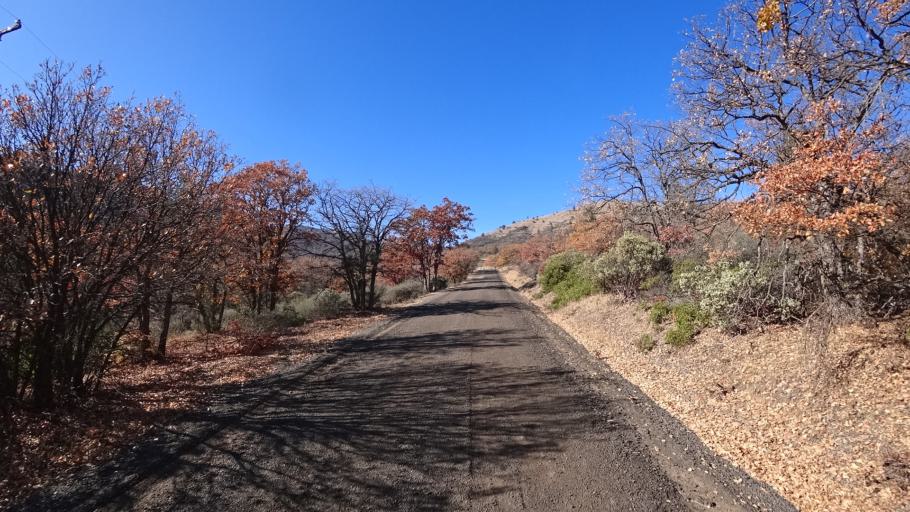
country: US
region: California
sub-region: Siskiyou County
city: Yreka
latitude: 41.7745
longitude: -122.6498
